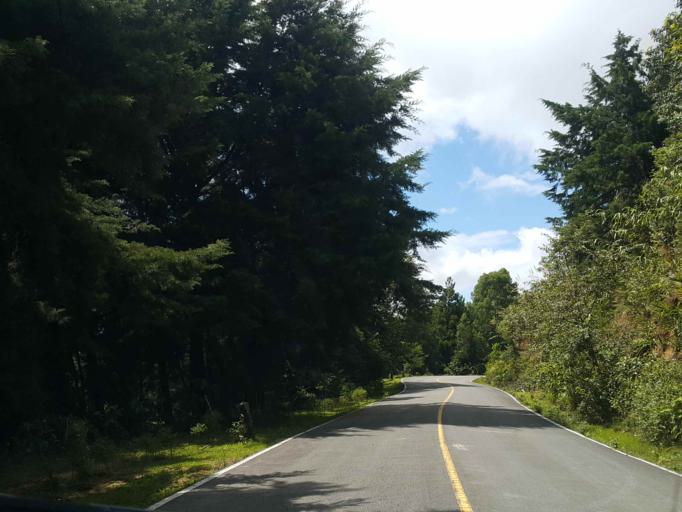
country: TH
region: Chiang Mai
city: Mae Chaem
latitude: 18.5159
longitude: 98.5300
